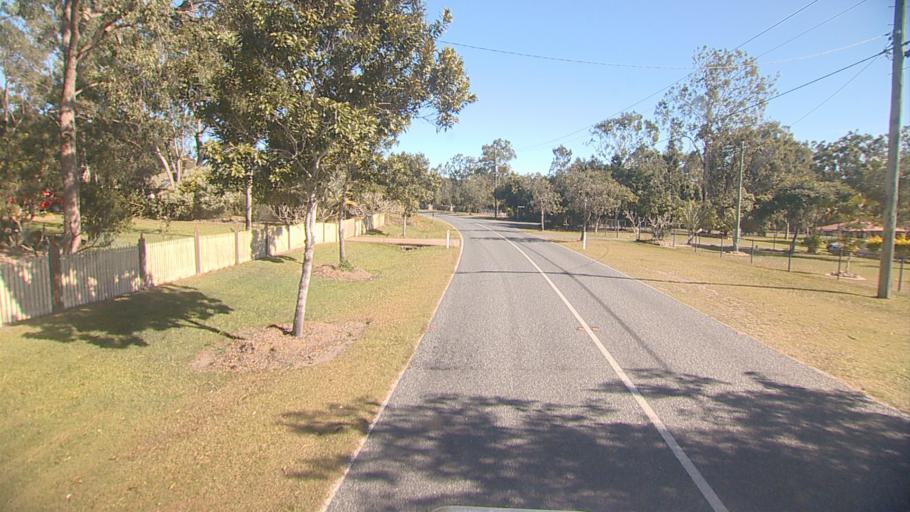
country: AU
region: Queensland
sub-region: Logan
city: North Maclean
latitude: -27.7417
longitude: 152.9570
